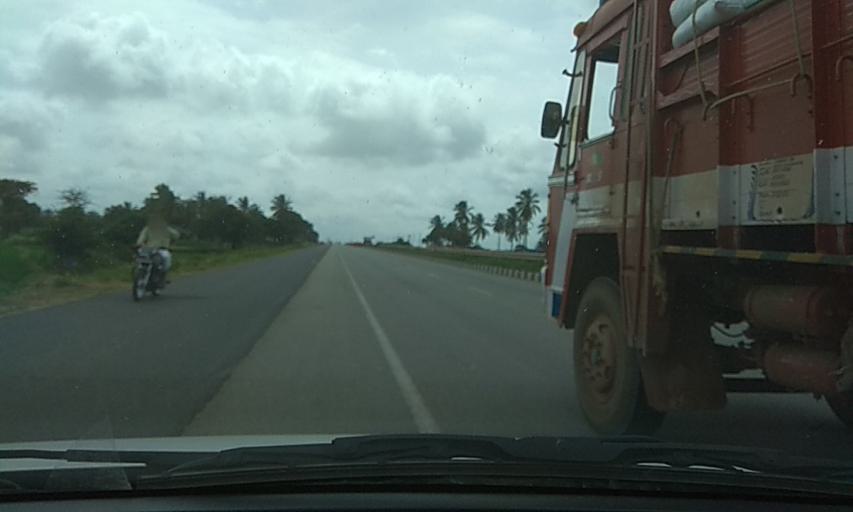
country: IN
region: Karnataka
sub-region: Davanagere
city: Harihar
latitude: 14.4483
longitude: 75.8831
